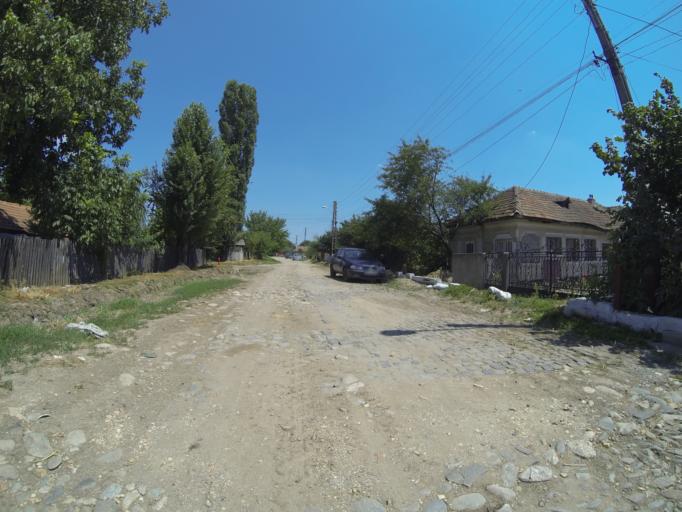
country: RO
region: Dolj
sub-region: Comuna Segarcea
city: Segarcea
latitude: 44.0871
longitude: 23.7427
